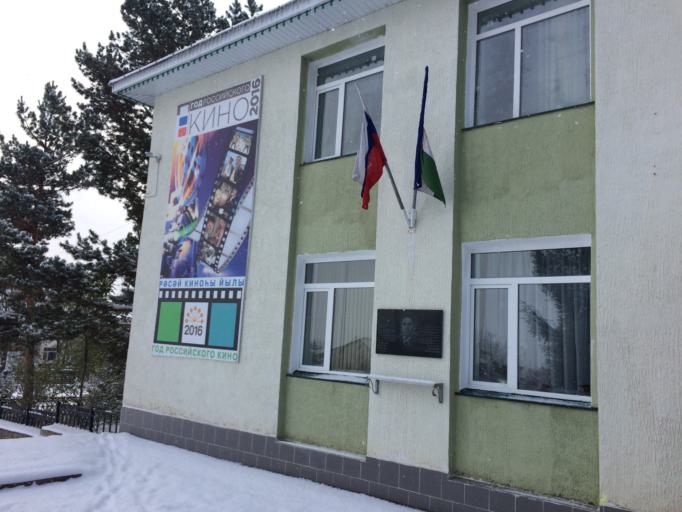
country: RU
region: Bashkortostan
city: Abzakovo
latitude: 53.3390
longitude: 58.5060
